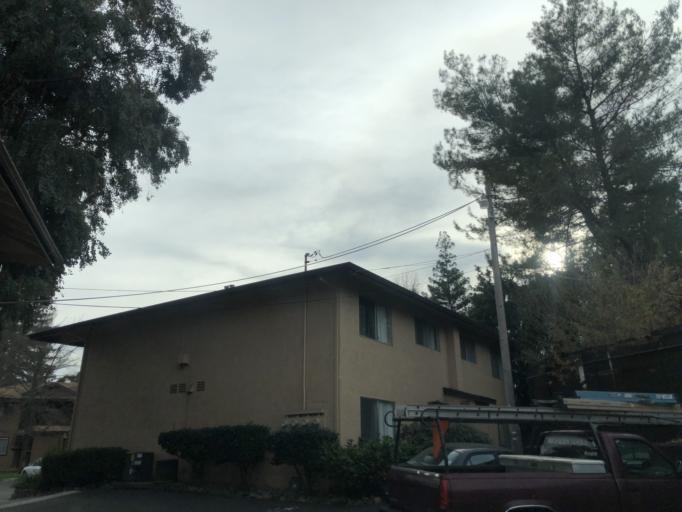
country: US
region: California
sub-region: Sacramento County
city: Foothill Farms
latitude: 38.6725
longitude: -121.3236
